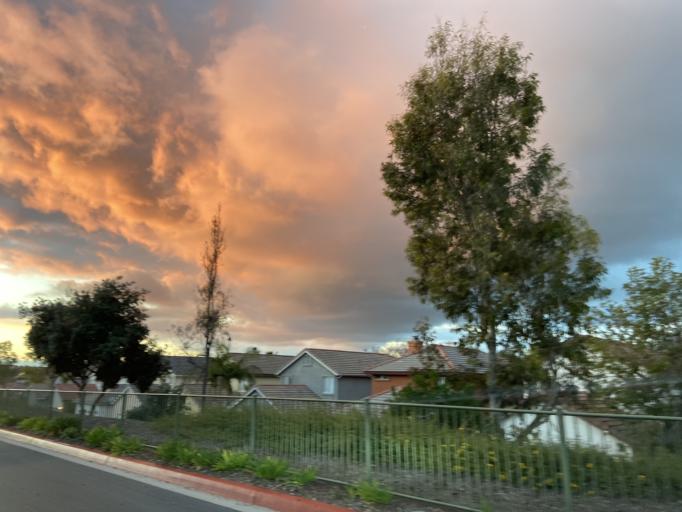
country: US
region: California
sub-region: San Diego County
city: Bonita
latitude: 32.6257
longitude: -116.9724
